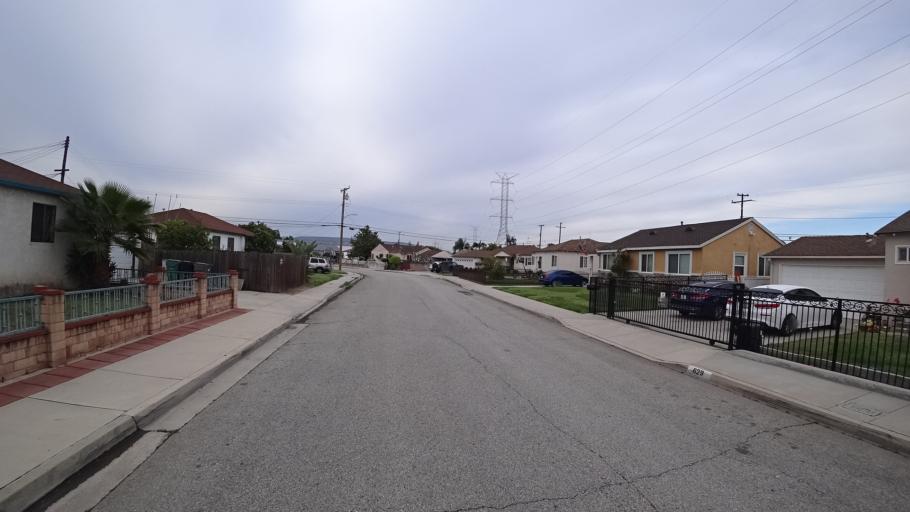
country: US
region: California
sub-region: Los Angeles County
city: Avocado Heights
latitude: 34.0632
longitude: -117.9969
